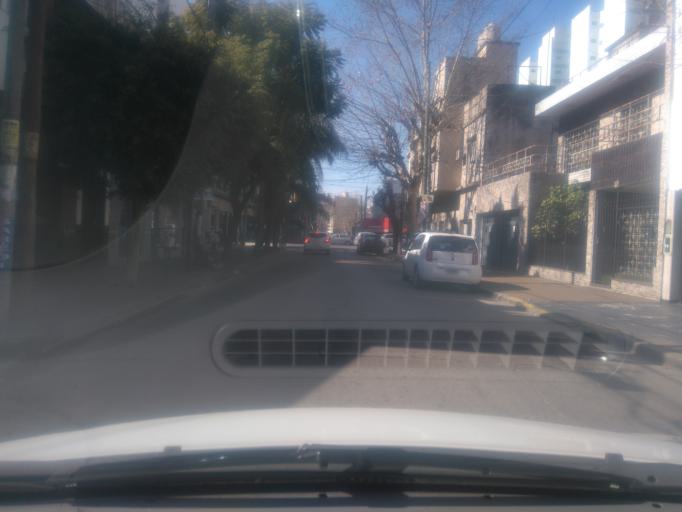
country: AR
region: Buenos Aires
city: San Justo
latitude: -34.6455
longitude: -58.5654
